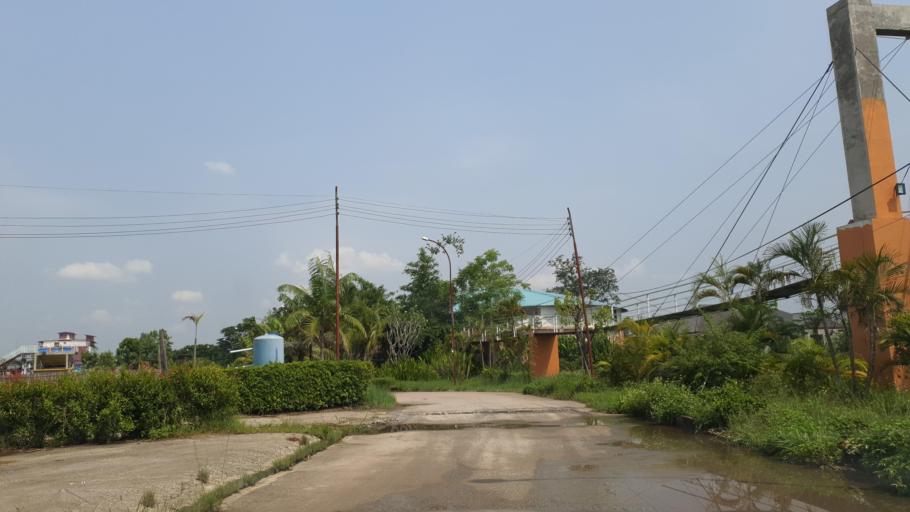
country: TH
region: Lamphun
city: Lamphun
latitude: 18.6030
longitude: 99.0134
